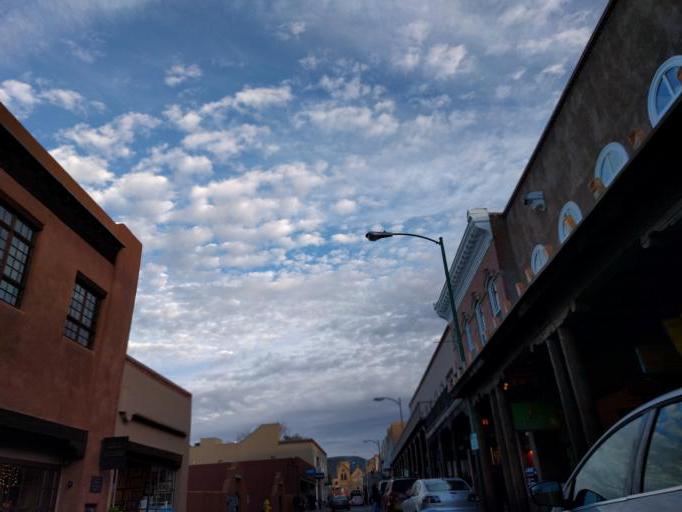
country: US
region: New Mexico
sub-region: Santa Fe County
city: Santa Fe
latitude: 35.6874
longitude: -105.9402
